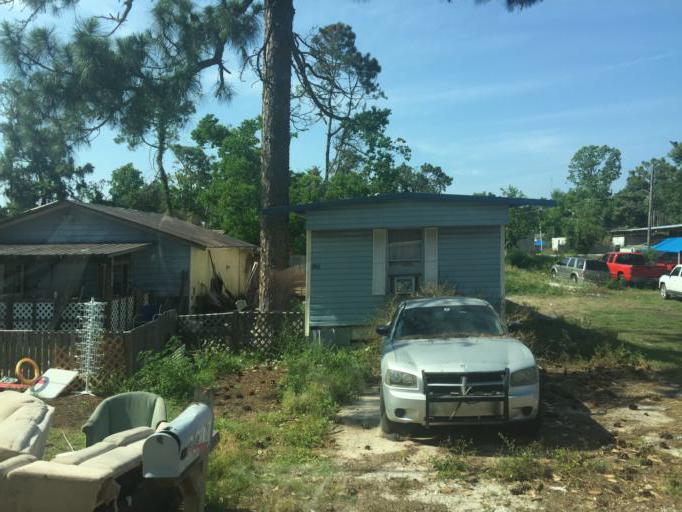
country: US
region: Florida
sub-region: Bay County
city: Panama City Beach
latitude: 30.1749
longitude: -85.7790
